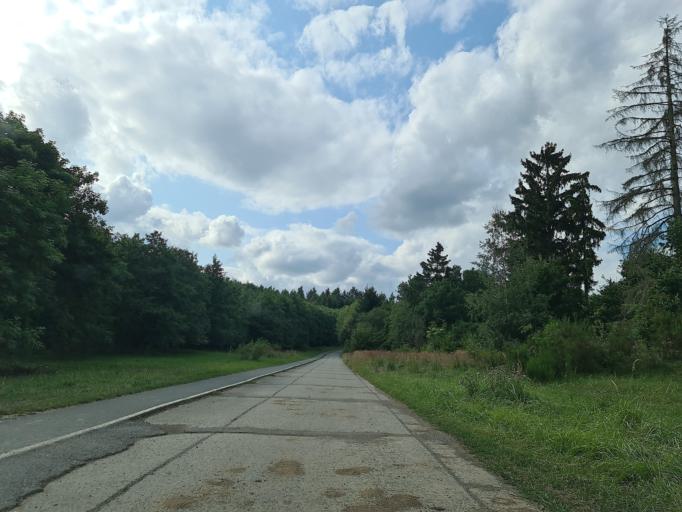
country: DE
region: Saxony
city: Syrau
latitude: 50.5036
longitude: 12.0682
